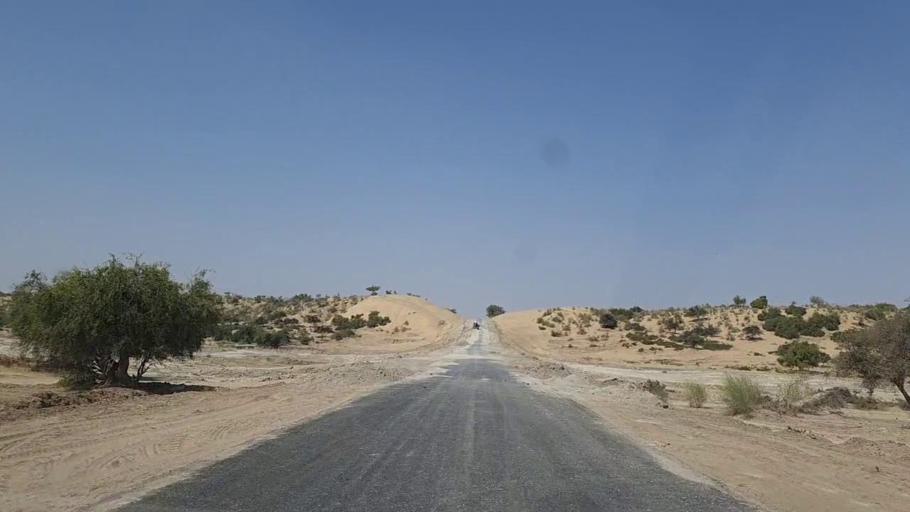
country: PK
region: Sindh
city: Diplo
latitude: 24.5862
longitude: 69.5602
